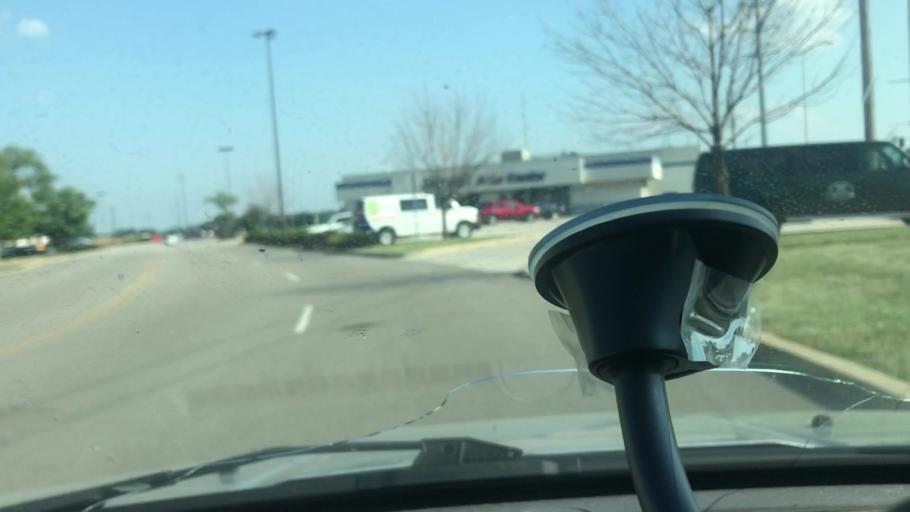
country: US
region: Illinois
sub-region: Peoria County
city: West Peoria
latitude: 40.7424
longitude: -89.6322
